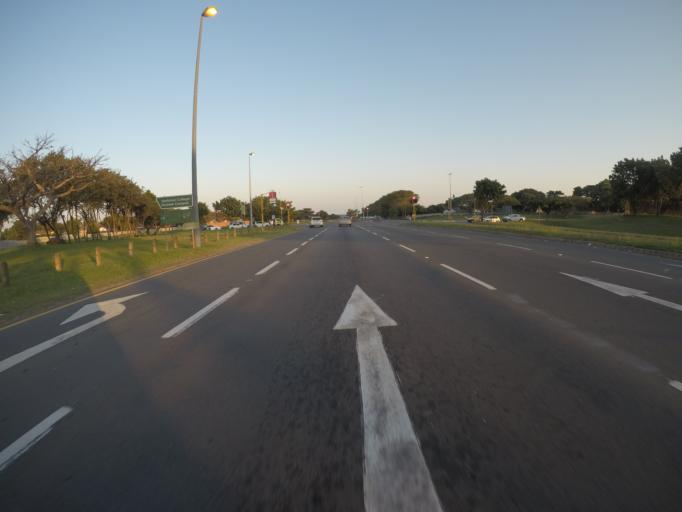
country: ZA
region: KwaZulu-Natal
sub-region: uThungulu District Municipality
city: Richards Bay
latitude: -28.7610
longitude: 32.0590
